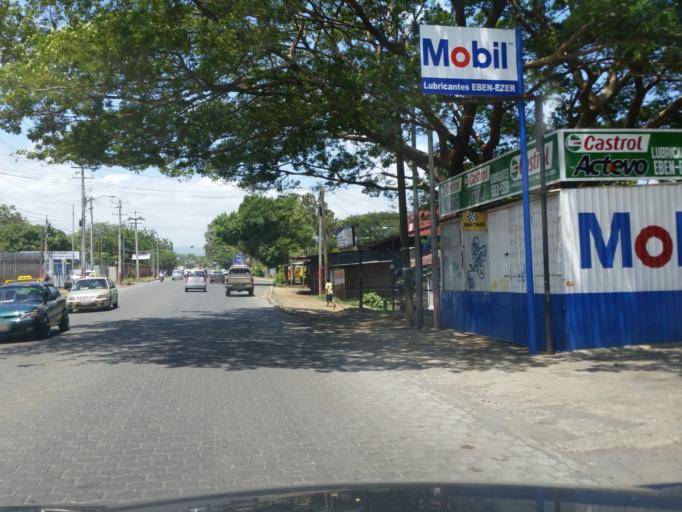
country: NI
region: Managua
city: Managua
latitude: 12.1313
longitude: -86.2008
